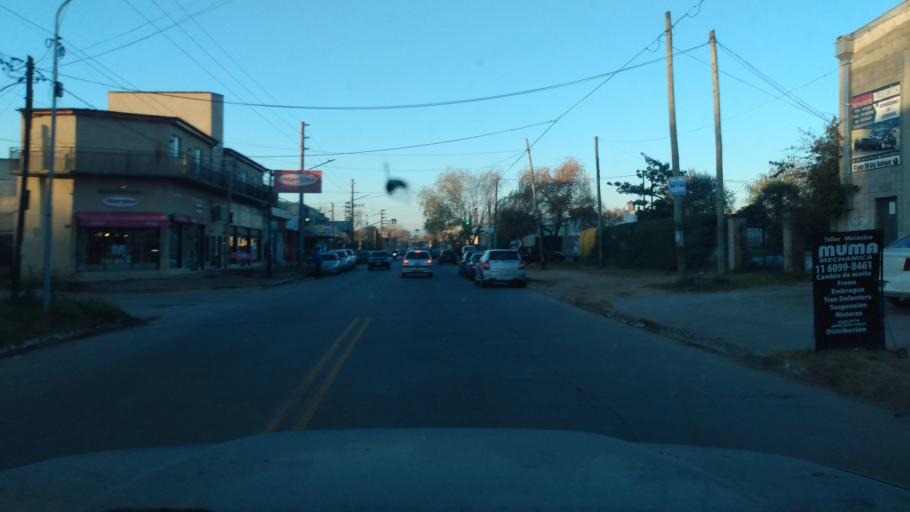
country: AR
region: Buenos Aires
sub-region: Partido de General Rodriguez
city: General Rodriguez
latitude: -34.5994
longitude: -58.9433
